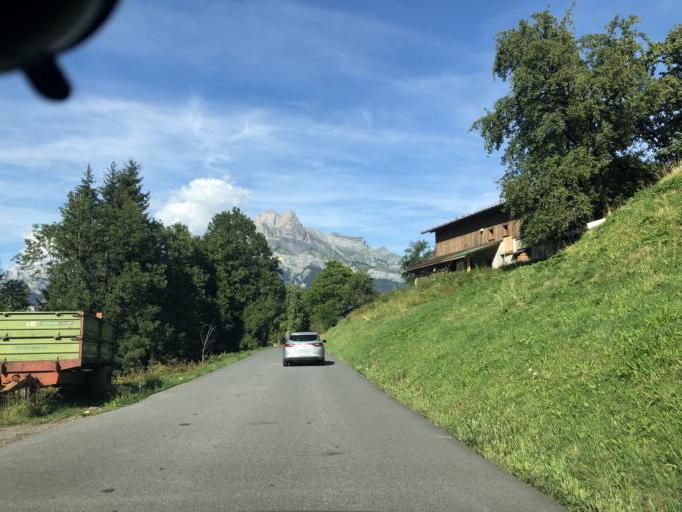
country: FR
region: Rhone-Alpes
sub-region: Departement de la Haute-Savoie
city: Cordon
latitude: 45.9133
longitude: 6.6114
